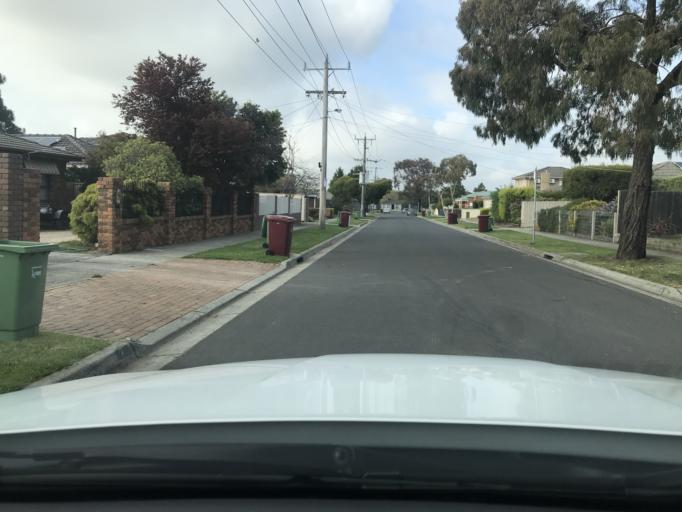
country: AU
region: Victoria
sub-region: Hume
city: Craigieburn
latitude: -37.6005
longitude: 144.9368
